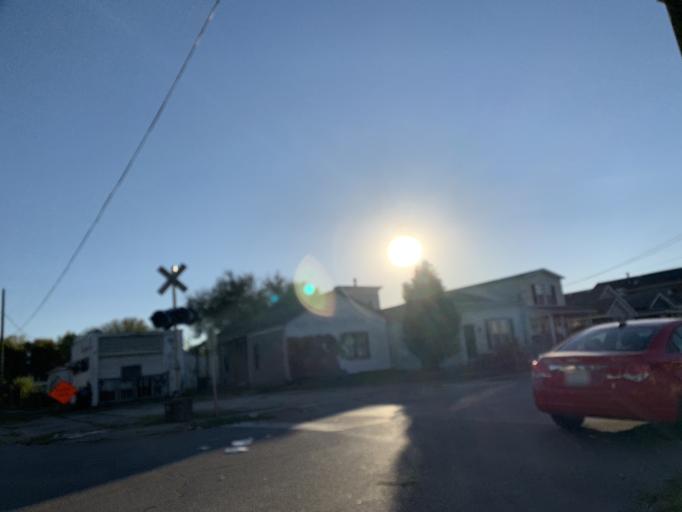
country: US
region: Indiana
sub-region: Floyd County
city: New Albany
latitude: 38.2742
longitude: -85.7942
